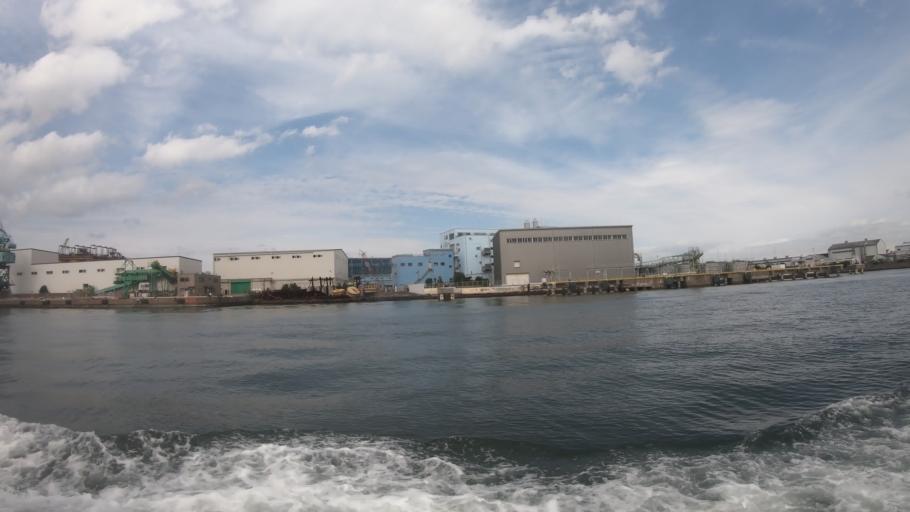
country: JP
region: Kanagawa
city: Yokohama
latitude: 35.4757
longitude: 139.6606
